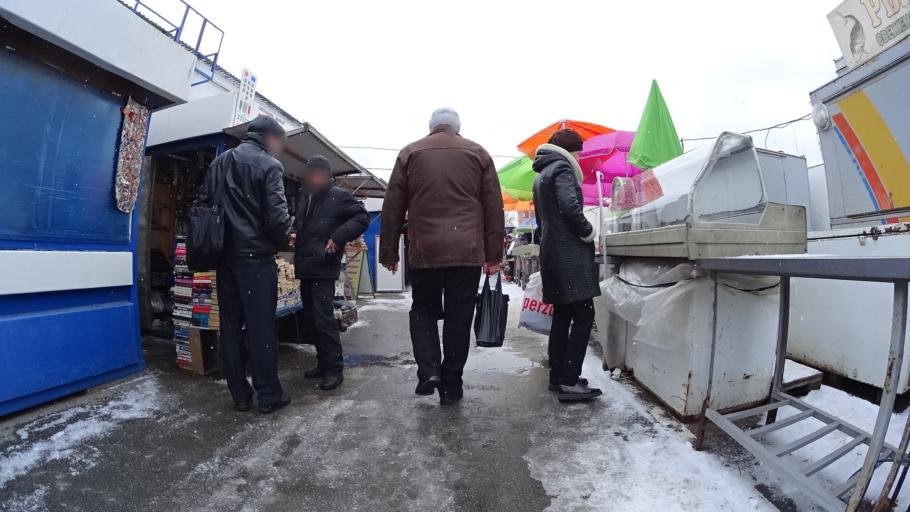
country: RU
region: Chelyabinsk
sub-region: Gorod Chelyabinsk
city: Chelyabinsk
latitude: 55.1899
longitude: 61.3187
